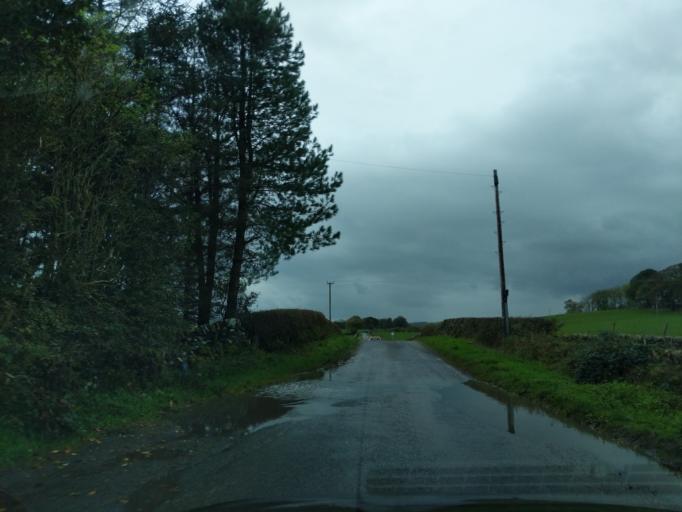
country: GB
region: Scotland
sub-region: Dumfries and Galloway
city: Castle Douglas
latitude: 54.9126
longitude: -3.9718
